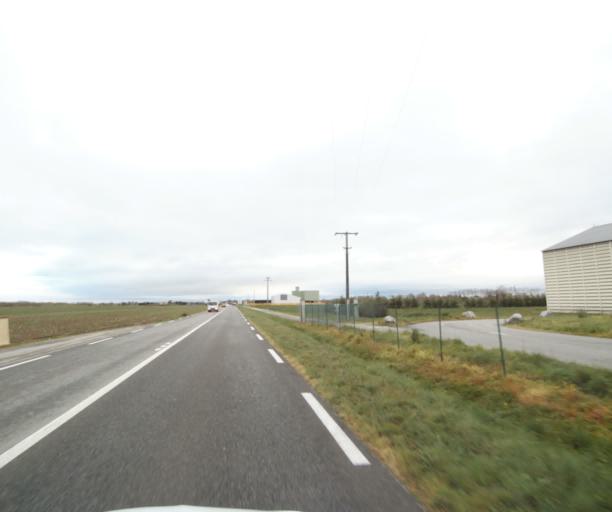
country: FR
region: Midi-Pyrenees
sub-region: Departement de l'Ariege
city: Saverdun
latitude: 43.1994
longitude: 1.6097
